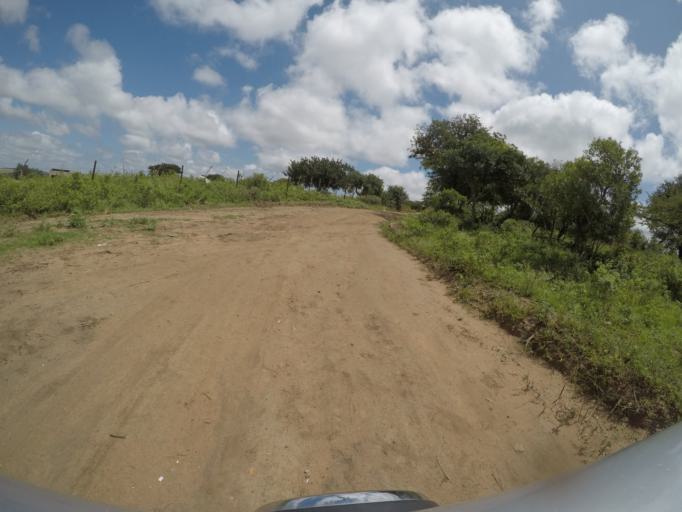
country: ZA
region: KwaZulu-Natal
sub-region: uThungulu District Municipality
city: Empangeni
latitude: -28.5844
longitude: 31.8364
